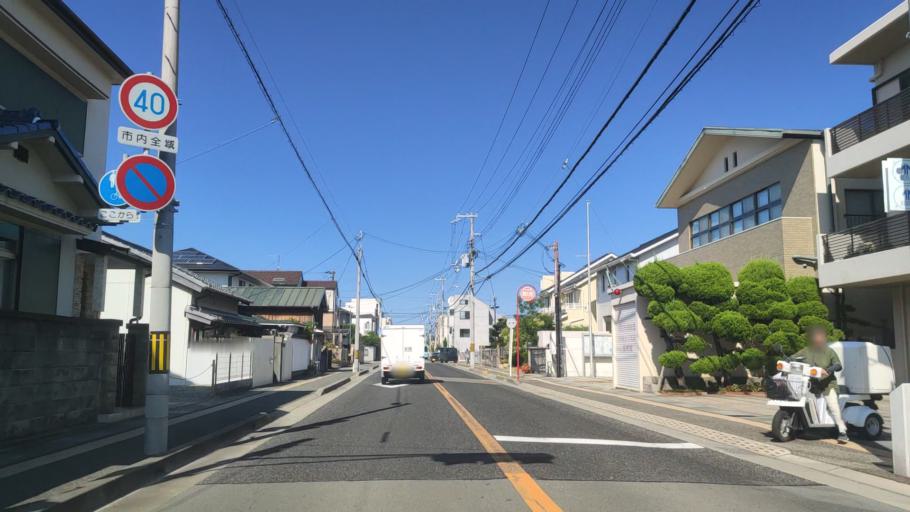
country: JP
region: Hyogo
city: Akashi
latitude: 34.6534
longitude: 135.0022
